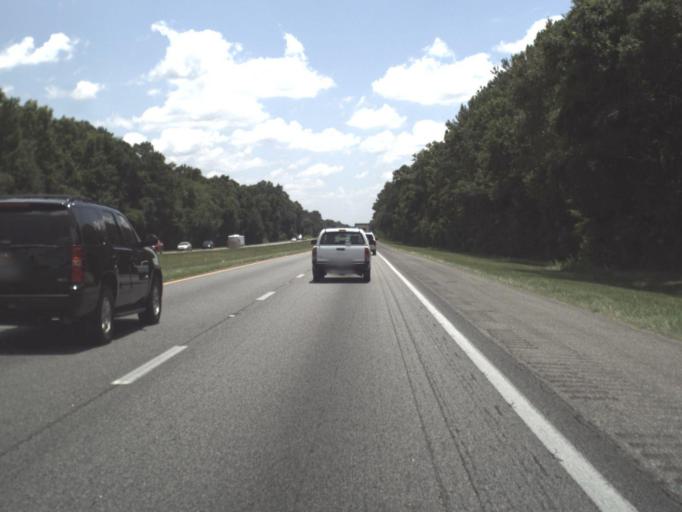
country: US
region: Florida
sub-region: Madison County
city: Madison
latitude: 30.4312
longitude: -83.6031
